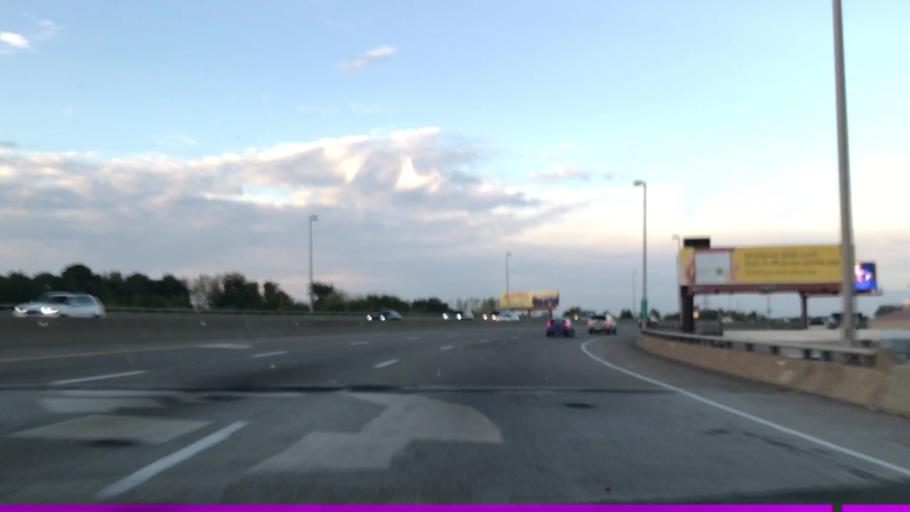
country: US
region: Virginia
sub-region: City of Richmond
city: Richmond
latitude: 37.5761
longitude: -77.4767
